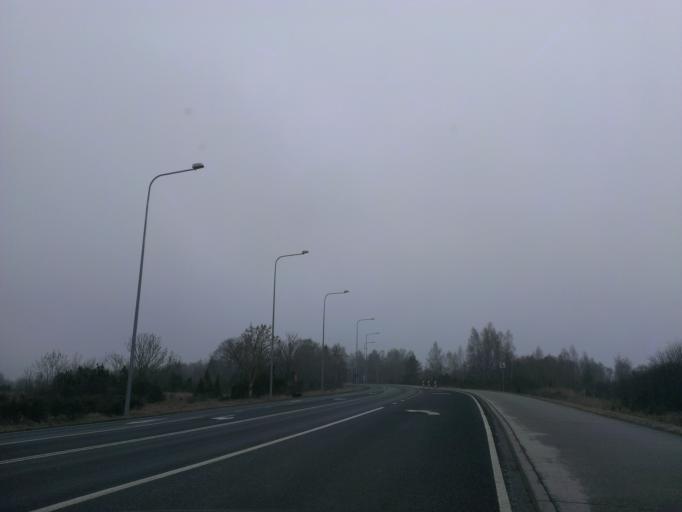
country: EE
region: Laeaene
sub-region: Lihula vald
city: Lihula
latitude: 58.5873
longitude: 23.5291
